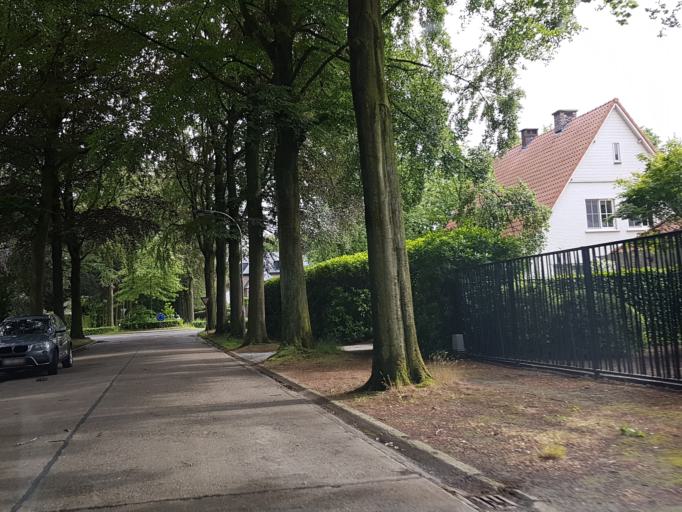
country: BE
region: Flanders
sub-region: Provincie Antwerpen
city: Kapellen
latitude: 51.2901
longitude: 4.4574
